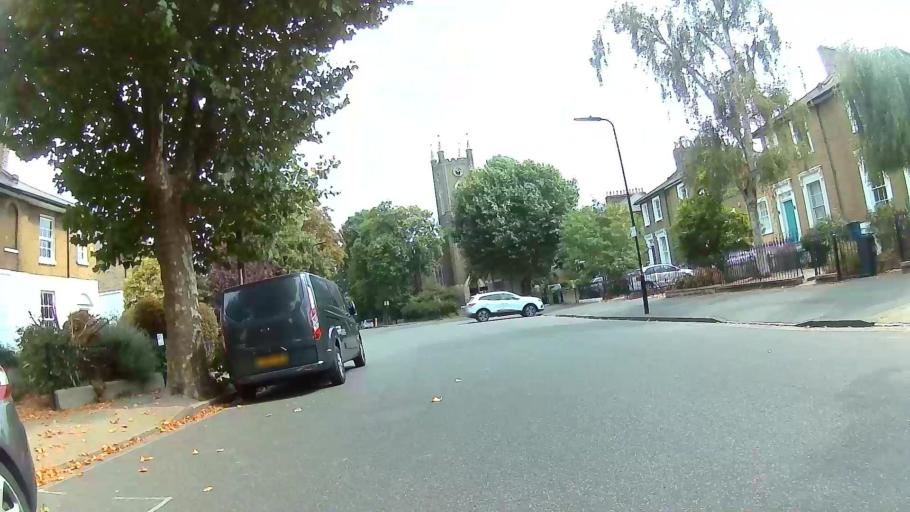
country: GB
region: England
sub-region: Greater London
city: Islington
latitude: 51.5411
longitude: -0.0816
